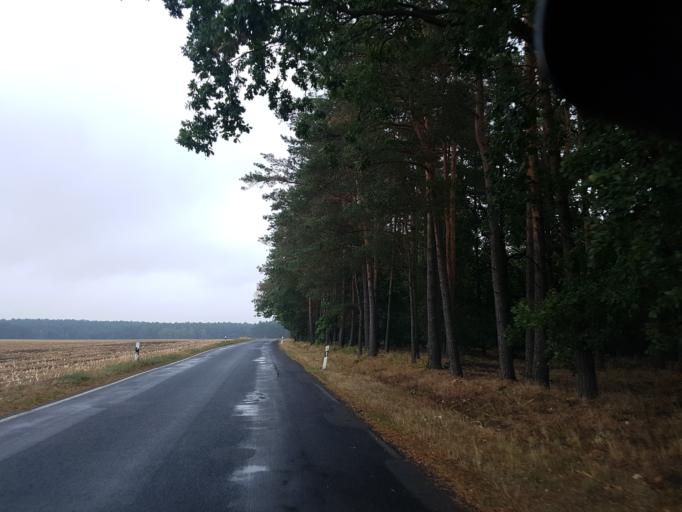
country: DE
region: Brandenburg
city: Gorzke
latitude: 52.1533
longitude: 12.3355
